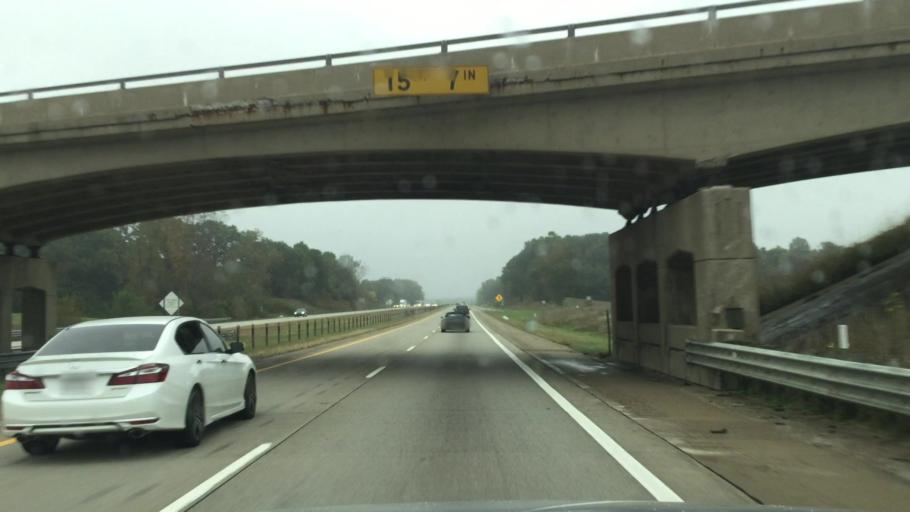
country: US
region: Michigan
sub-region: Van Buren County
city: Paw Paw
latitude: 42.1991
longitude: -85.9663
